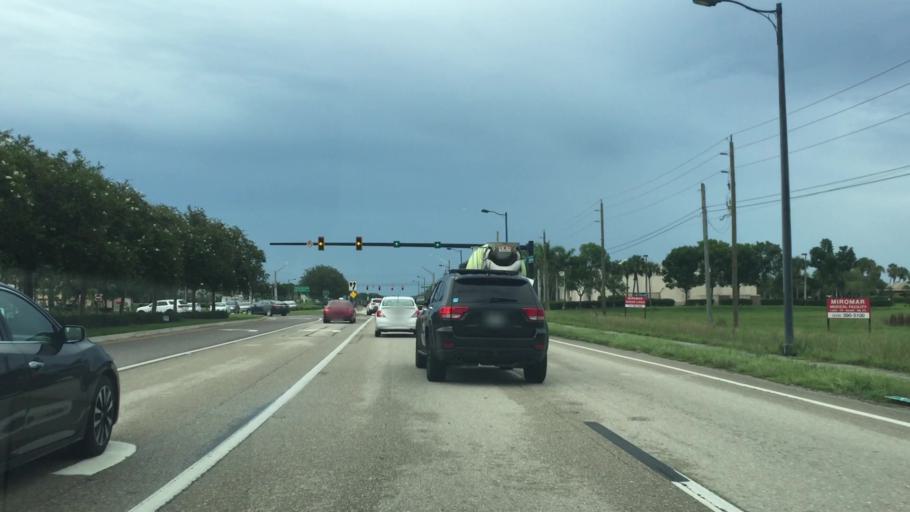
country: US
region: Florida
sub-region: Lee County
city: Estero
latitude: 26.4348
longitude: -81.7725
